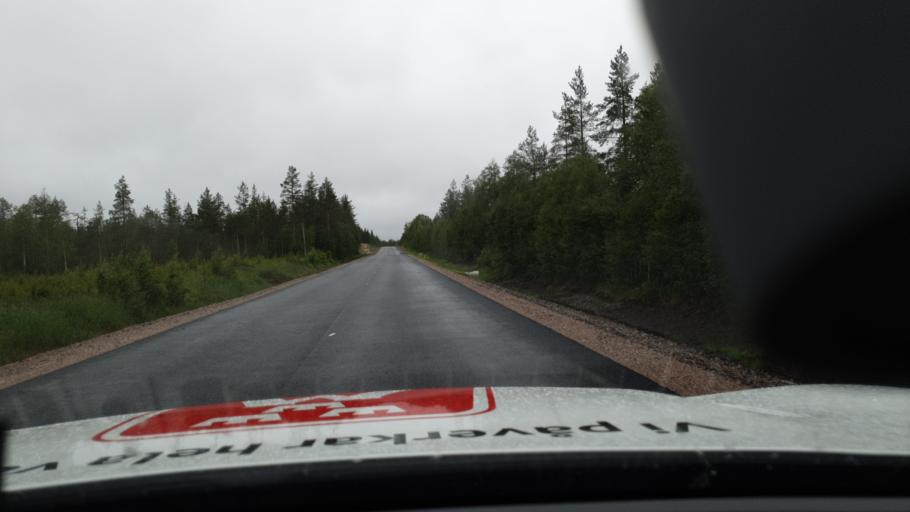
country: SE
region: Norrbotten
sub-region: Overtornea Kommun
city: OEvertornea
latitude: 66.5347
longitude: 23.3643
